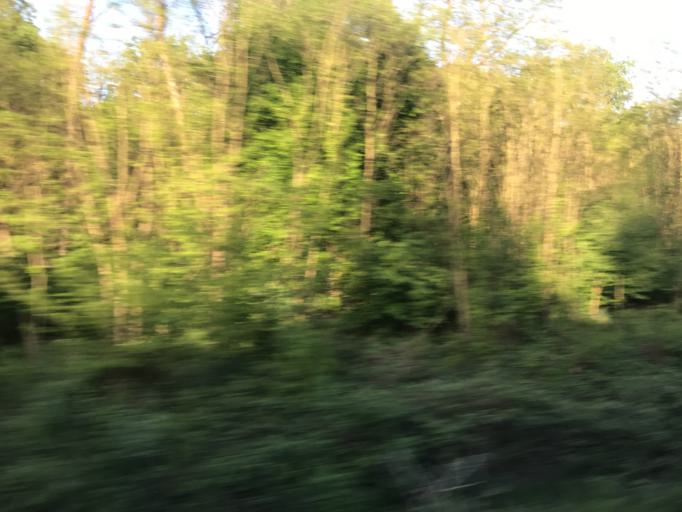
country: DE
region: Rheinland-Pfalz
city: Dudenhofen
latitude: 49.3523
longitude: 8.3996
